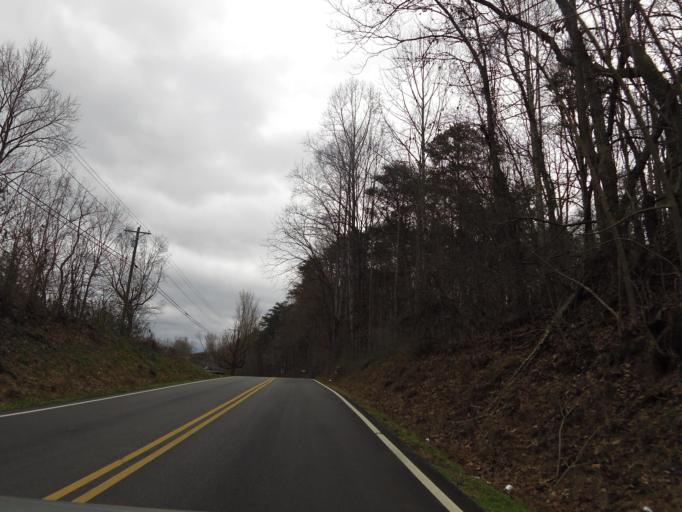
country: US
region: Tennessee
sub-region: Grainger County
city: Rutledge
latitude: 36.2081
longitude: -83.5703
